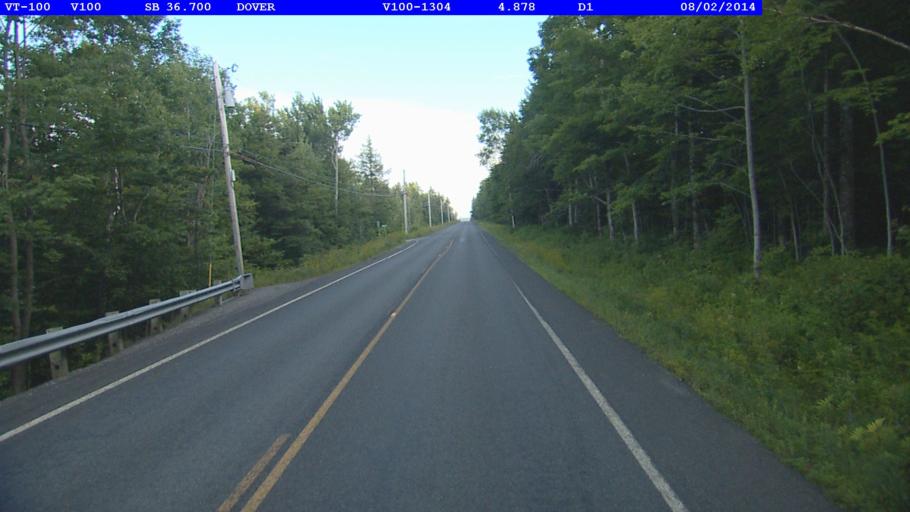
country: US
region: Vermont
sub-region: Windham County
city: Dover
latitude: 42.9815
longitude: -72.8887
